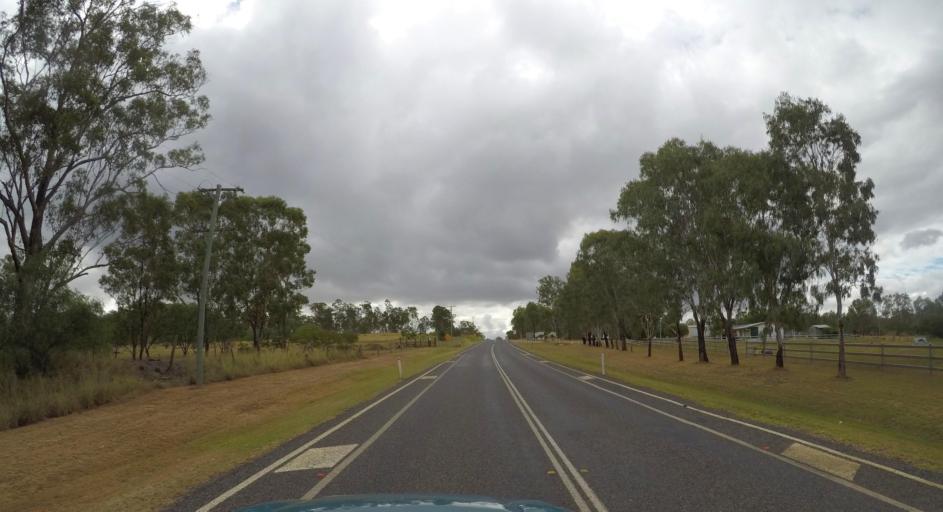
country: AU
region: Queensland
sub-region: North Burnett
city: Gayndah
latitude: -25.3634
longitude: 151.1201
